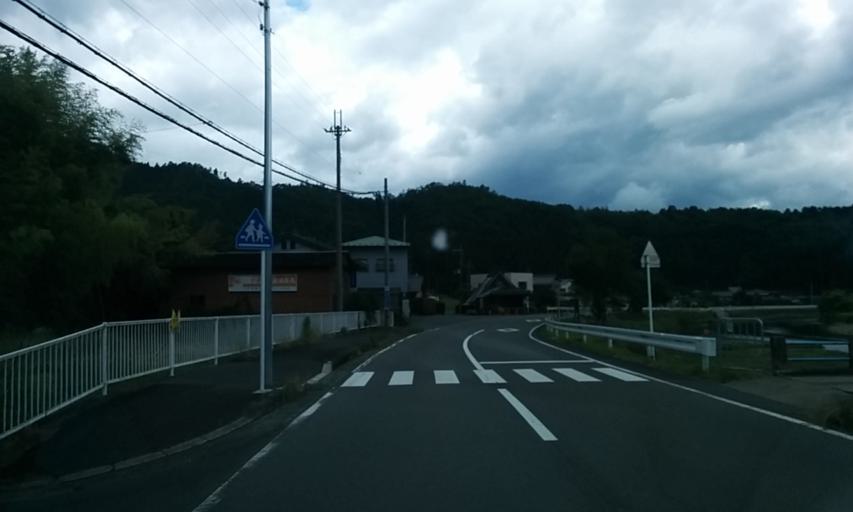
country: JP
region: Kyoto
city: Kameoka
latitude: 35.1020
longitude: 135.4351
